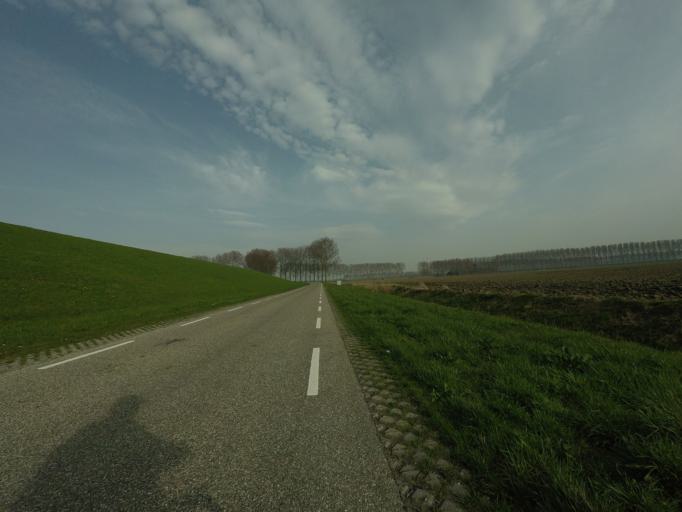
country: NL
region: Zeeland
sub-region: Gemeente Terneuzen
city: Zaamslag
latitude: 51.3627
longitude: 3.9373
